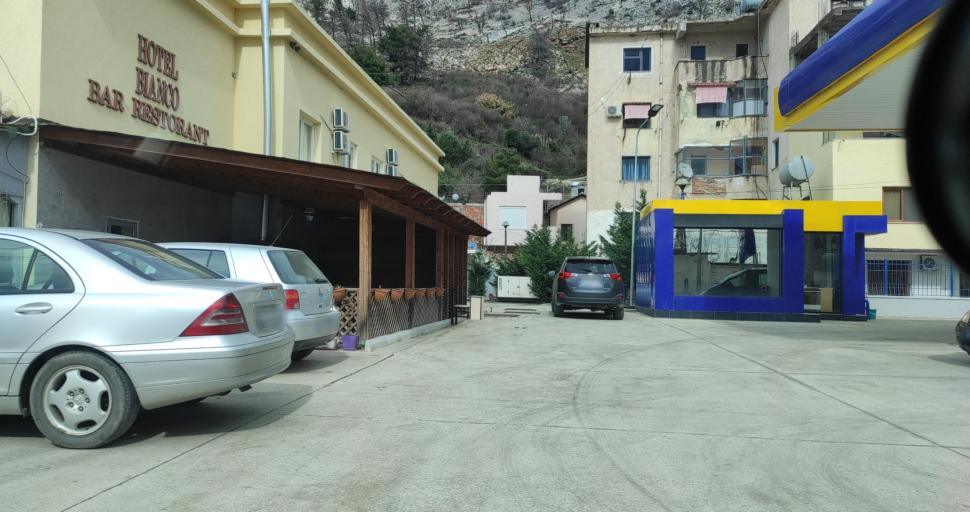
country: AL
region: Lezhe
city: Shengjin
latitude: 41.8149
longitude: 19.5907
